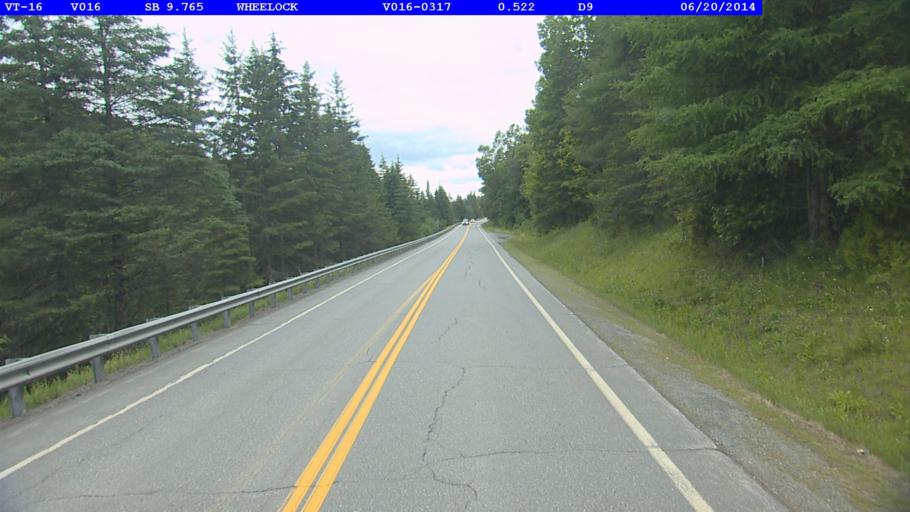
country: US
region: Vermont
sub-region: Caledonia County
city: Hardwick
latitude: 44.6049
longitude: -72.2089
